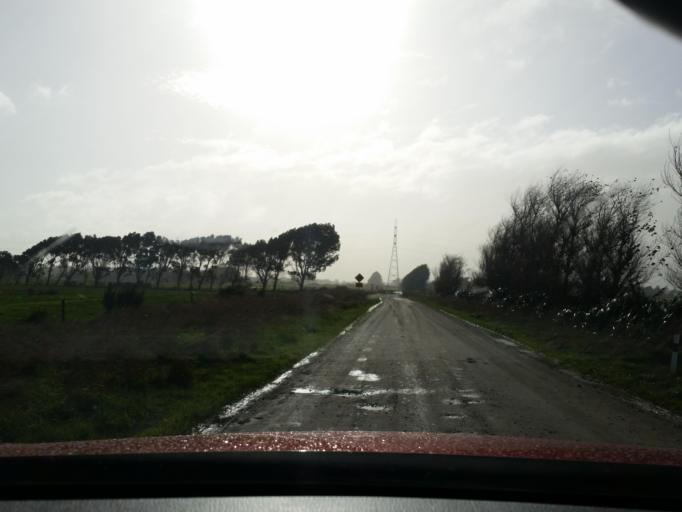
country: NZ
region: Southland
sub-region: Invercargill City
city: Invercargill
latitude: -46.3072
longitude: 168.4162
